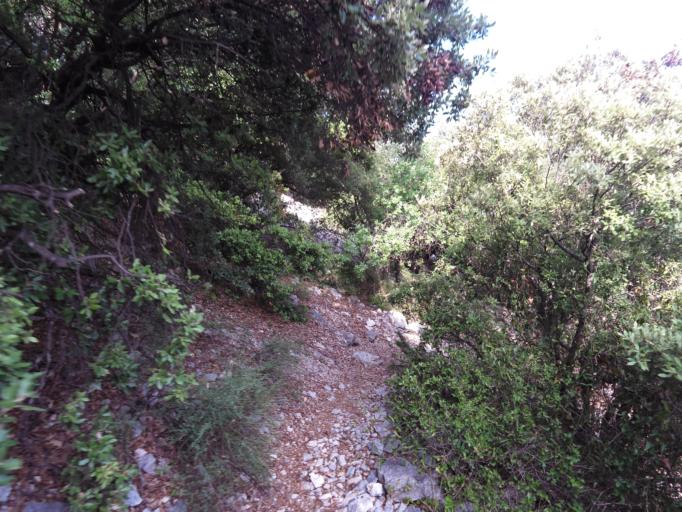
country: FR
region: Languedoc-Roussillon
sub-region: Departement de l'Herault
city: Saint-Mathieu-de-Treviers
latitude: 43.7923
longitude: 3.8225
